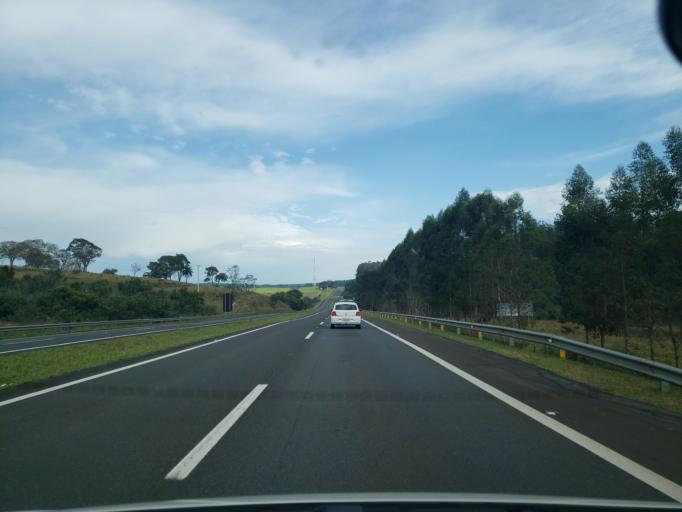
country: BR
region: Sao Paulo
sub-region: Itirapina
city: Itirapina
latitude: -22.2744
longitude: -47.9618
